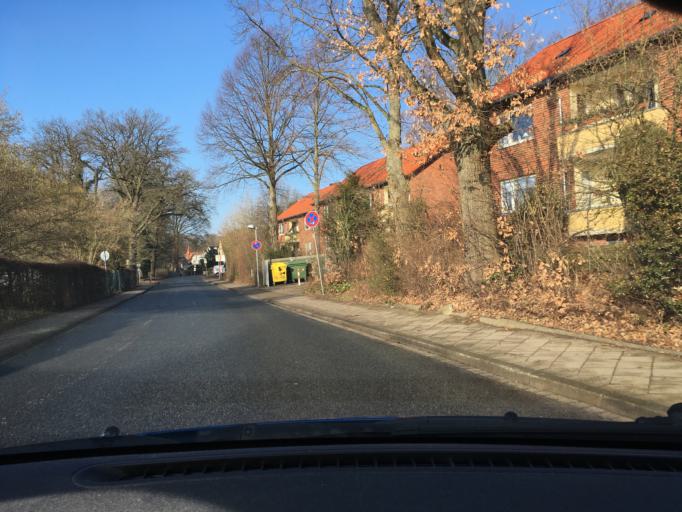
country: DE
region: Lower Saxony
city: Lueneburg
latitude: 53.2593
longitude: 10.4328
